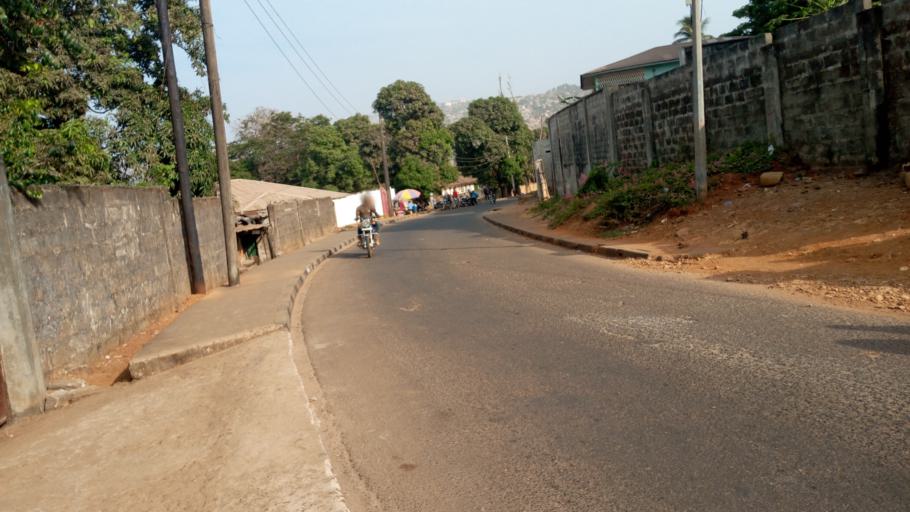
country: SL
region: Western Area
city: Freetown
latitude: 8.4802
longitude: -13.2586
